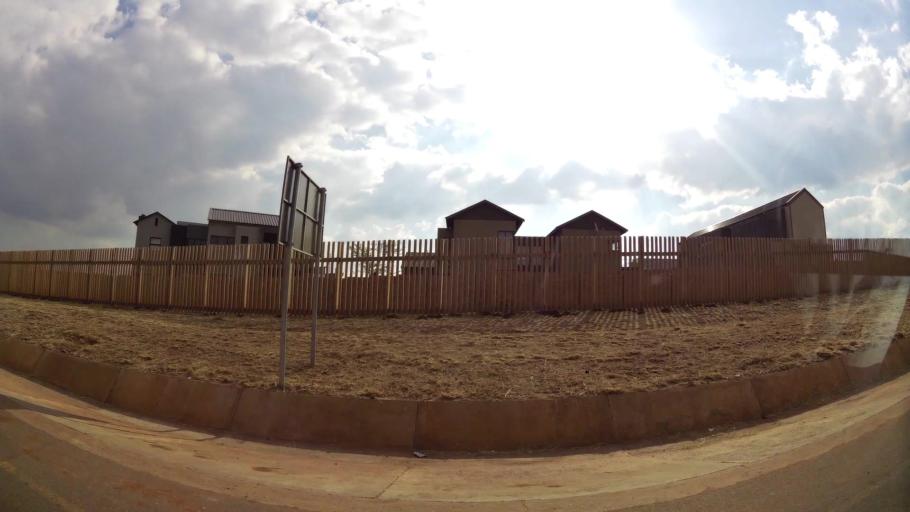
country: ZA
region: Gauteng
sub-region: Ekurhuleni Metropolitan Municipality
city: Tembisa
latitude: -25.9313
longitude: 28.2098
